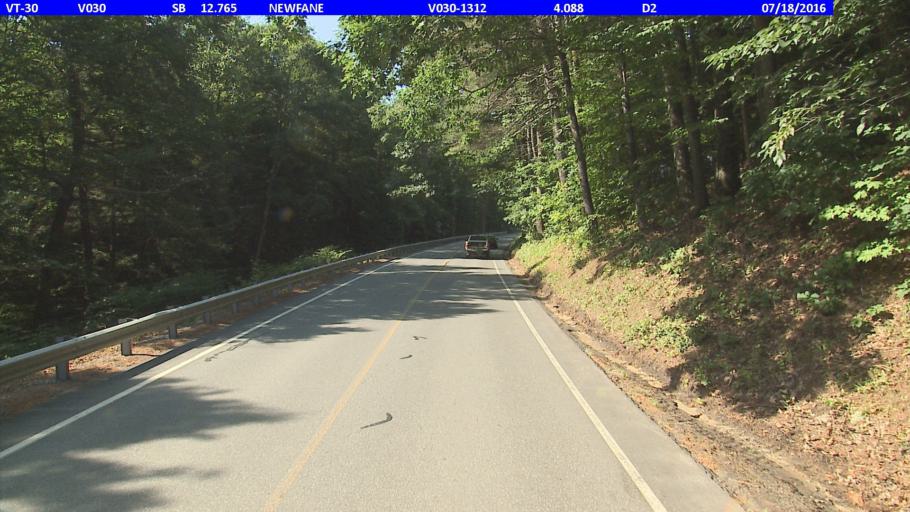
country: US
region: Vermont
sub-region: Windham County
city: Newfane
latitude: 43.0001
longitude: -72.6440
